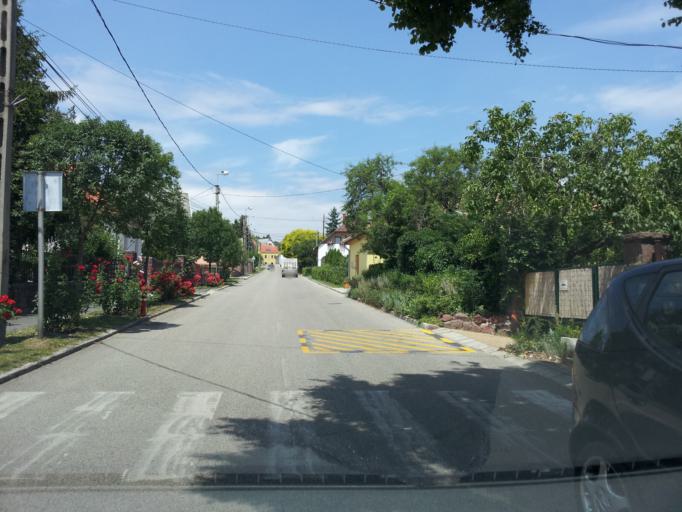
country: HU
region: Veszprem
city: Csopak
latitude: 46.9924
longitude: 17.9751
